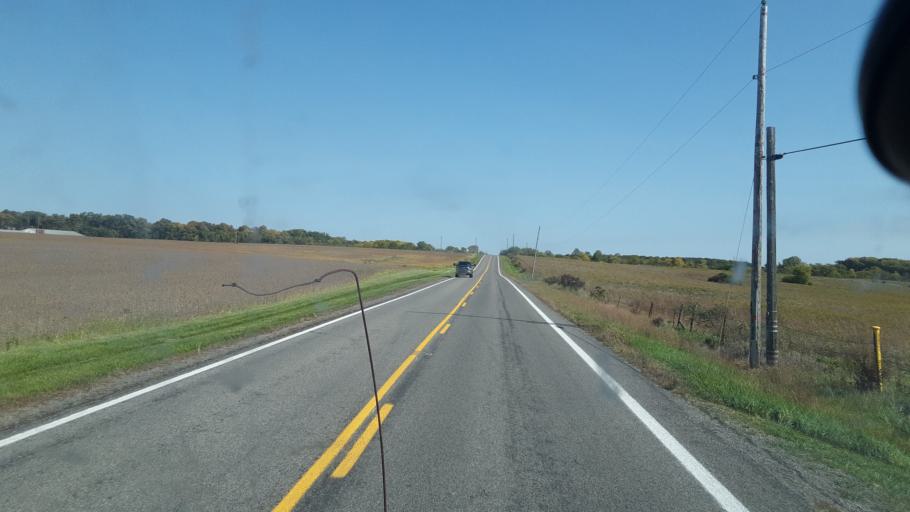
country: US
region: Ohio
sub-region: Logan County
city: Northwood
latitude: 40.5043
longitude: -83.6916
